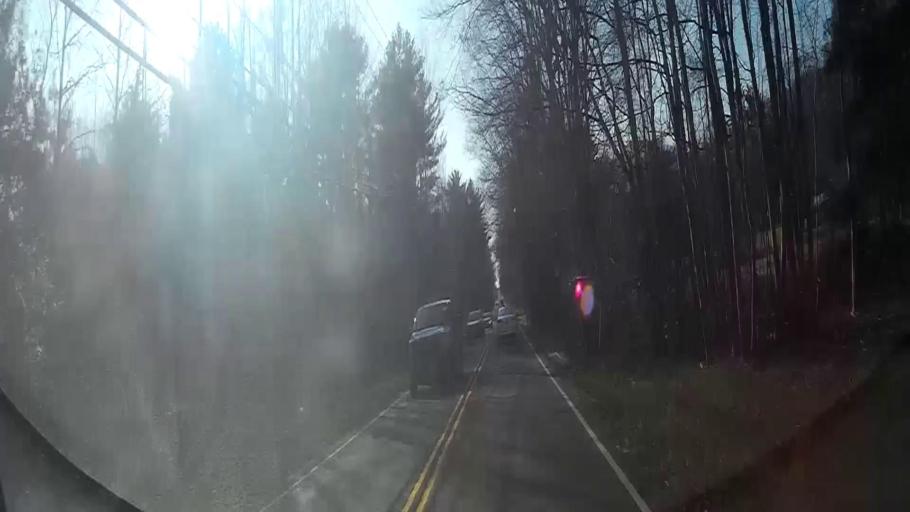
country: US
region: New Jersey
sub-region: Burlington County
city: Marlton
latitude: 39.8628
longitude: -74.8823
